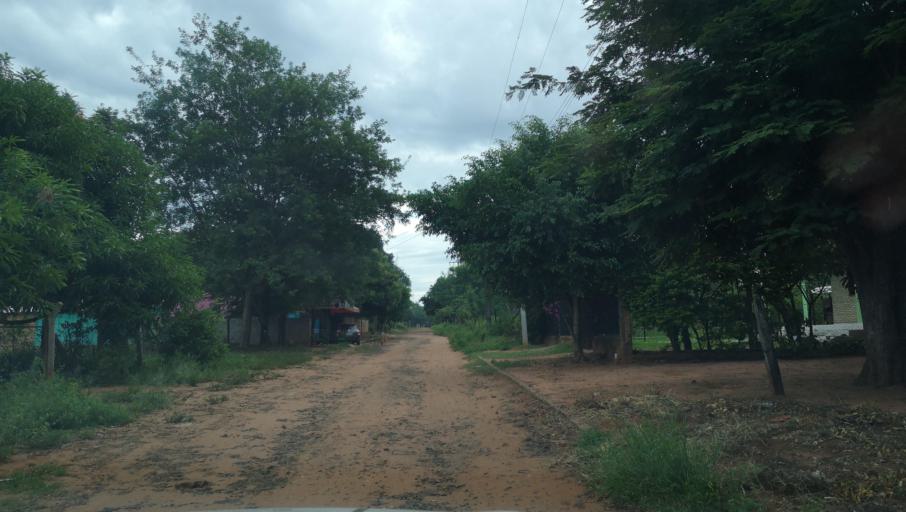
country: PY
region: San Pedro
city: Capiibary
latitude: -24.7239
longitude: -56.0183
